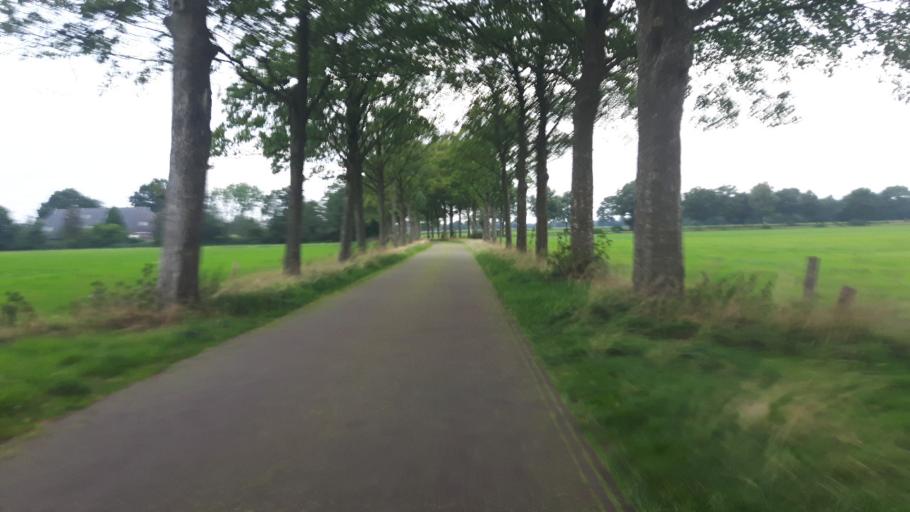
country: NL
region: Friesland
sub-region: Gemeente Heerenveen
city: Jubbega
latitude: 52.9762
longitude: 6.2362
